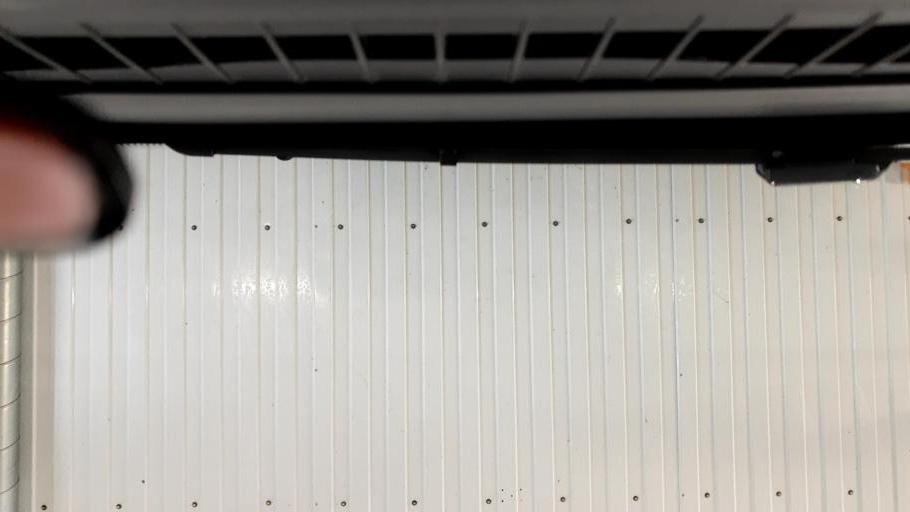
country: RU
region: Nizjnij Novgorod
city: Kstovo
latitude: 56.1381
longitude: 44.2014
